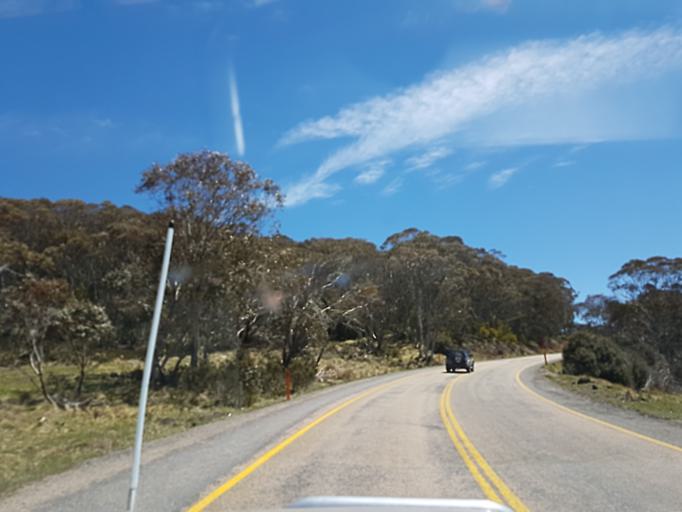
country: AU
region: Victoria
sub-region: Alpine
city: Mount Beauty
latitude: -37.0258
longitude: 147.2697
